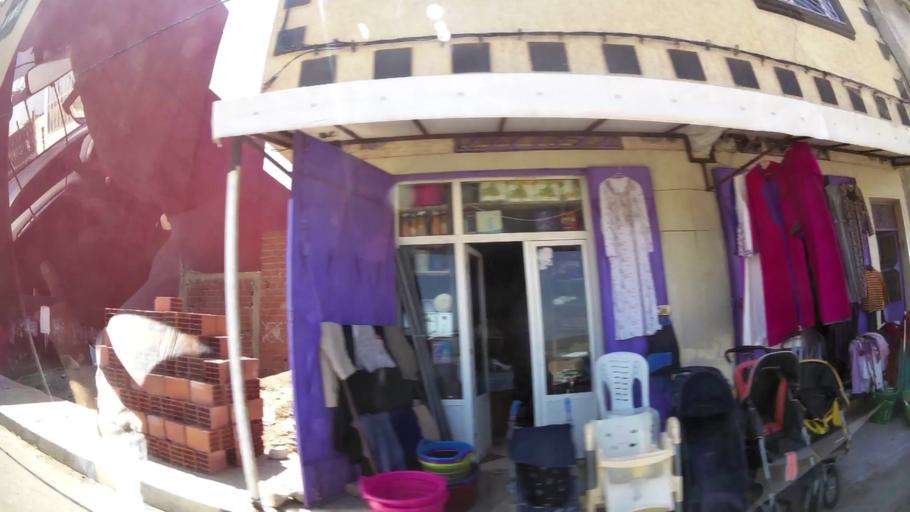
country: MA
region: Oriental
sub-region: Oujda-Angad
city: Oujda
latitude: 34.6832
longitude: -1.9594
